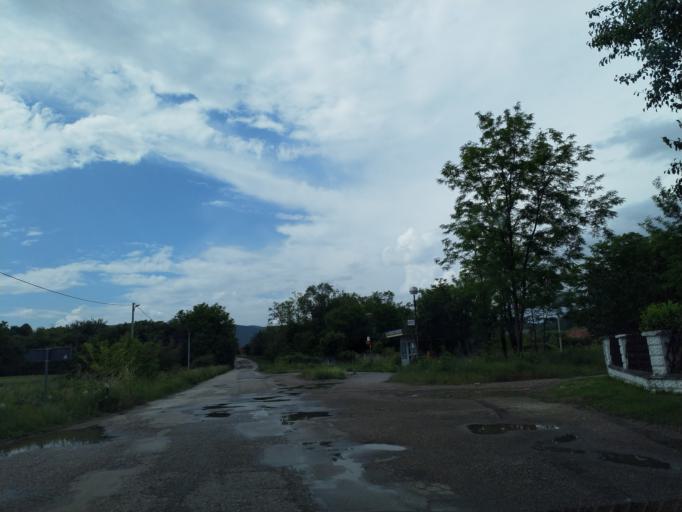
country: RS
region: Central Serbia
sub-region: Zajecarski Okrug
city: Boljevac
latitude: 43.8957
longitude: 21.9624
